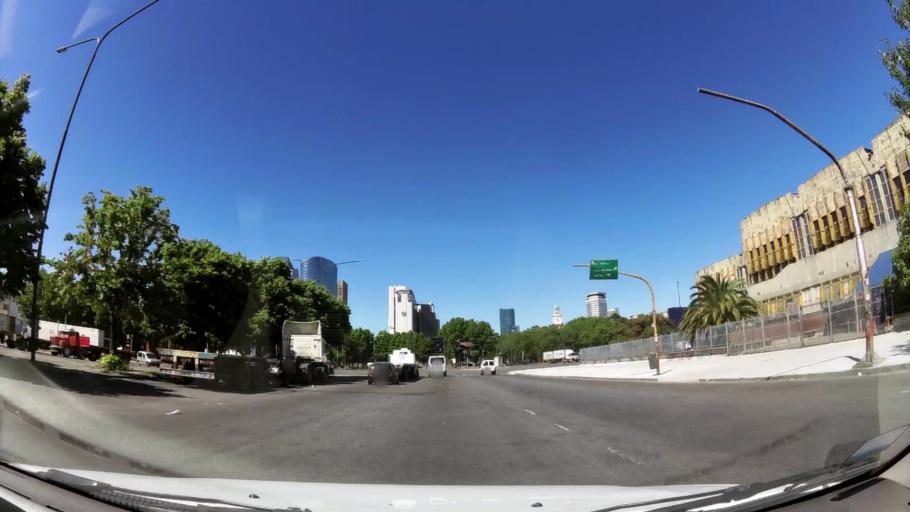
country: AR
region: Buenos Aires F.D.
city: Retiro
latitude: -34.5894
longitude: -58.3698
